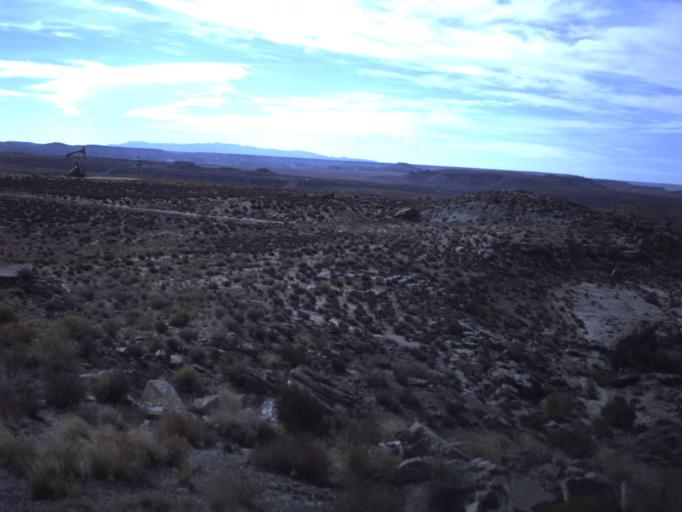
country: US
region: Utah
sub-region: San Juan County
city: Blanding
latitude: 37.3214
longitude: -109.3125
